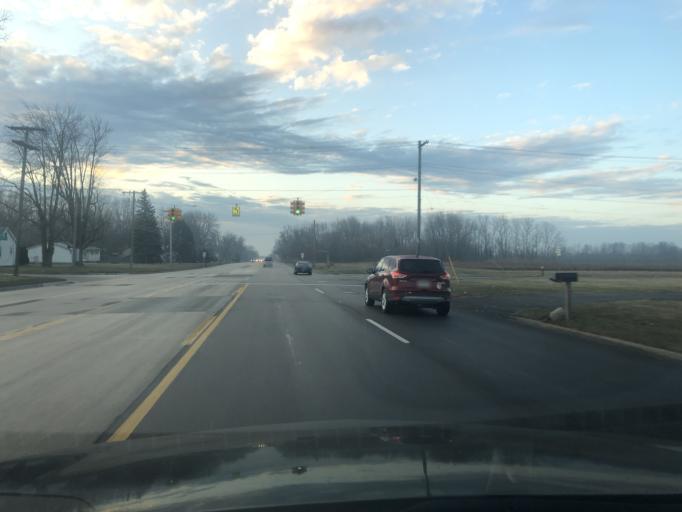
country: US
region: Michigan
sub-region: Wayne County
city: Wayne
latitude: 42.2606
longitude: -83.3480
